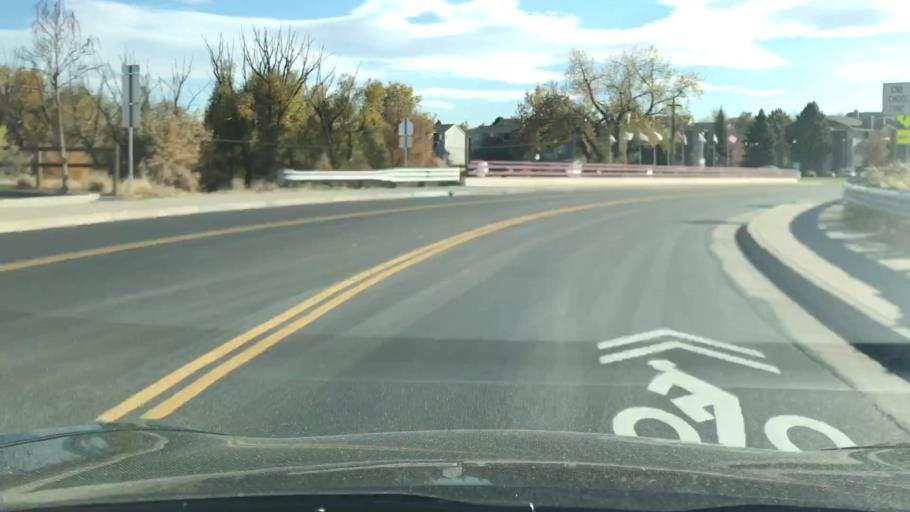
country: US
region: Colorado
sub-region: Arapahoe County
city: Glendale
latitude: 39.6710
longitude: -104.8898
